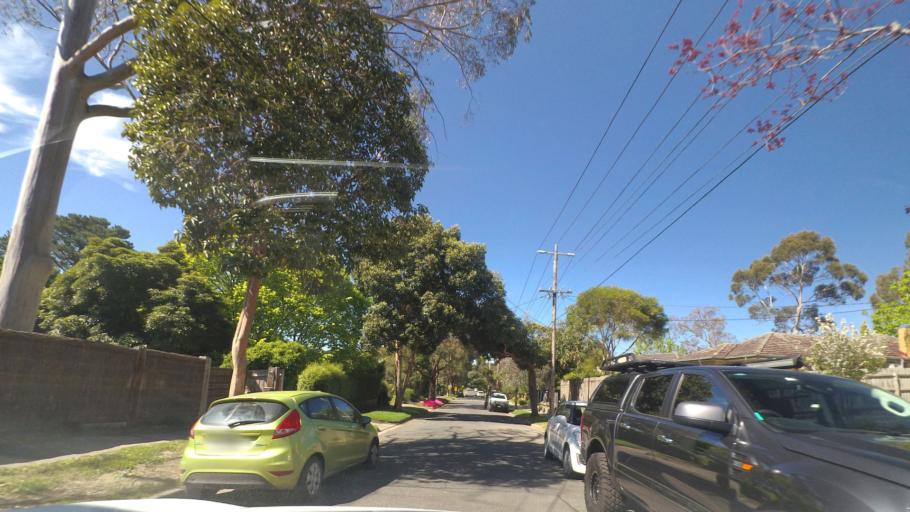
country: AU
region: Victoria
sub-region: Maroondah
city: Ringwood East
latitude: -37.8225
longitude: 145.2592
